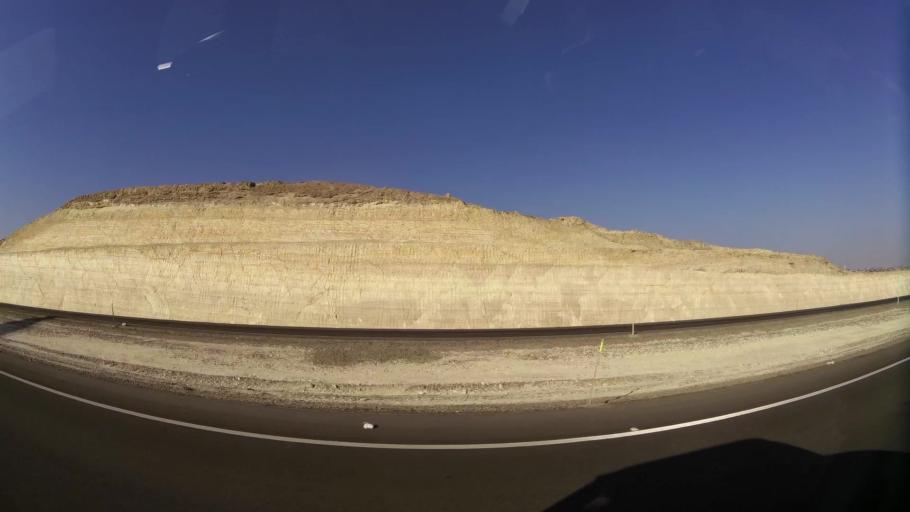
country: PE
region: Ica
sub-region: Provincia de Pisco
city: San Clemente
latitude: -13.6603
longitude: -76.1739
